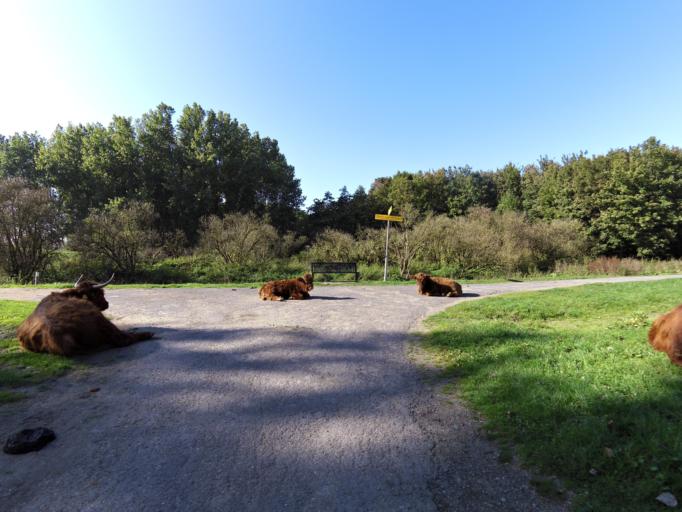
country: NL
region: South Holland
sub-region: Gemeente Vlaardingen
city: Vlaardingen
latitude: 51.9313
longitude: 4.3131
